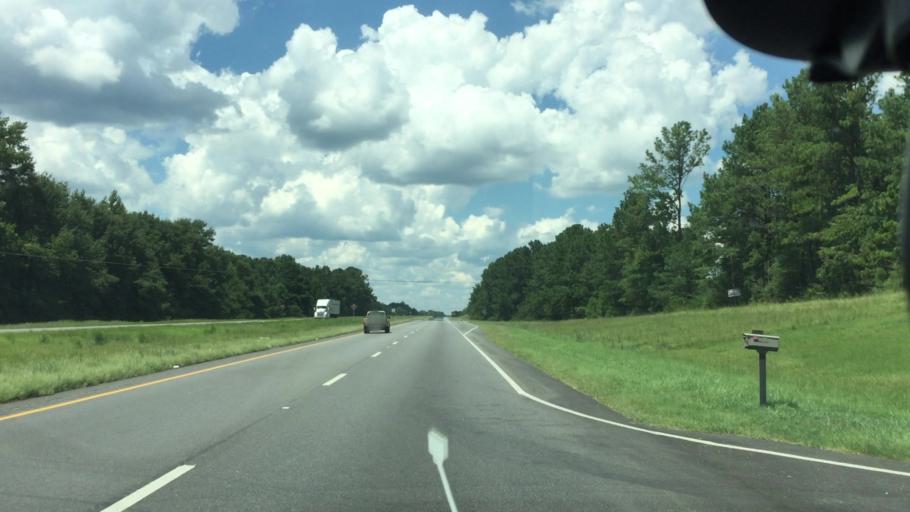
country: US
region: Alabama
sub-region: Pike County
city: Troy
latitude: 31.8765
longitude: -86.0030
